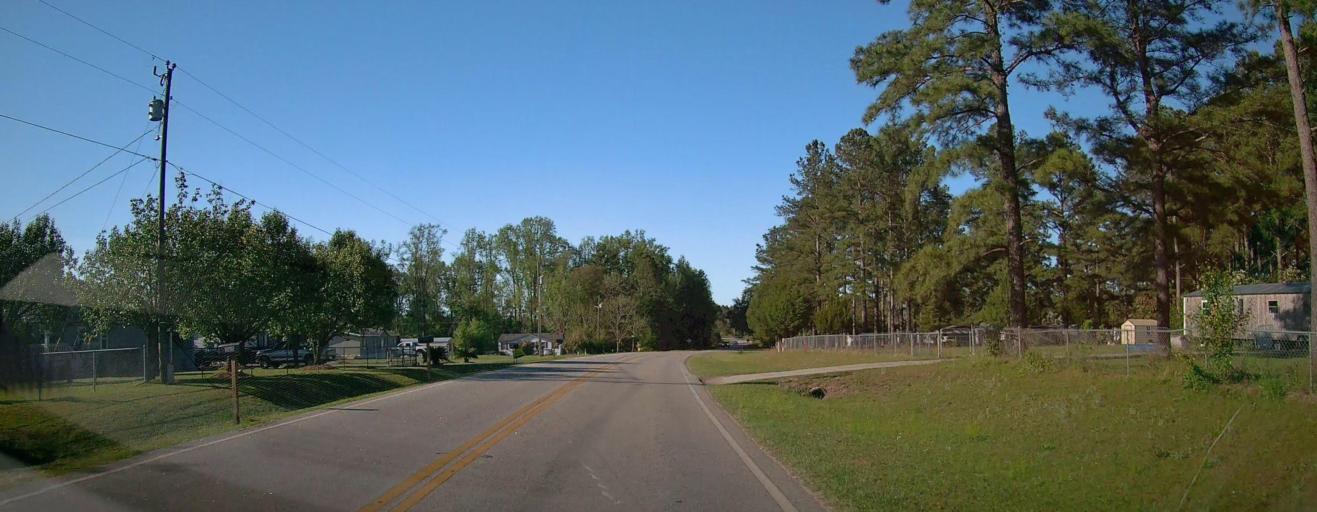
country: US
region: Georgia
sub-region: Ben Hill County
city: Fitzgerald
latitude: 31.7358
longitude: -83.2354
